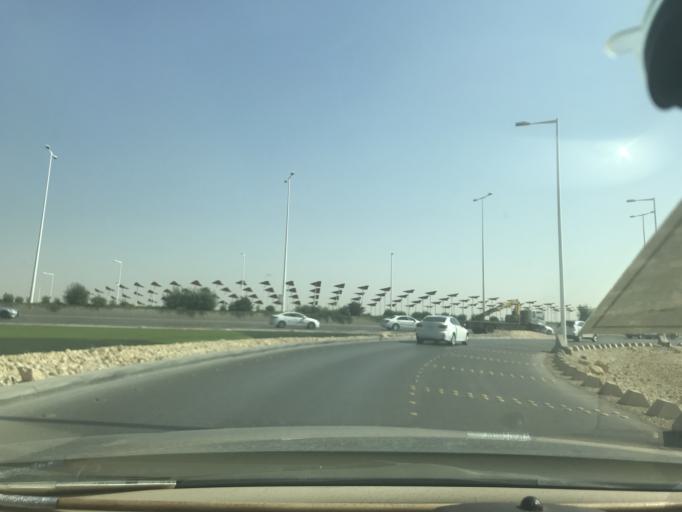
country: SA
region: Ar Riyad
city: Riyadh
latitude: 24.7284
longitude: 46.7092
